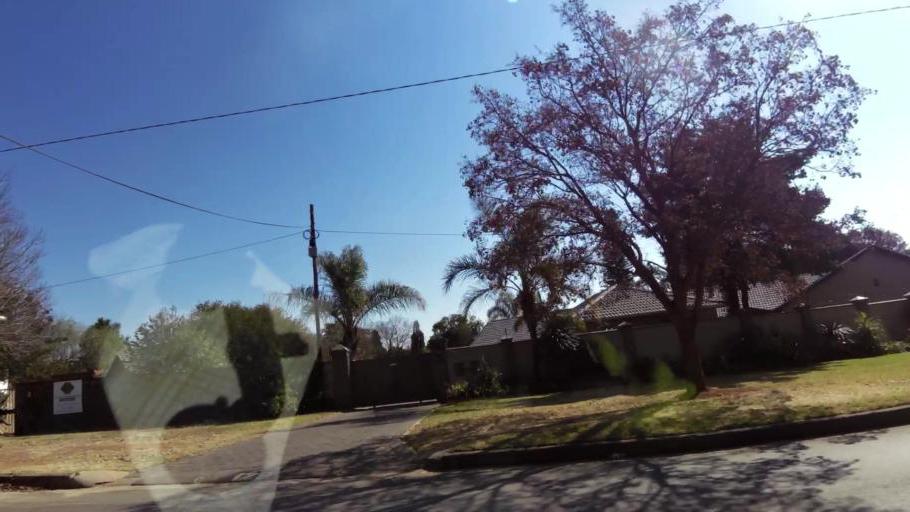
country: ZA
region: Gauteng
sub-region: City of Johannesburg Metropolitan Municipality
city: Roodepoort
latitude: -26.1388
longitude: 27.9393
